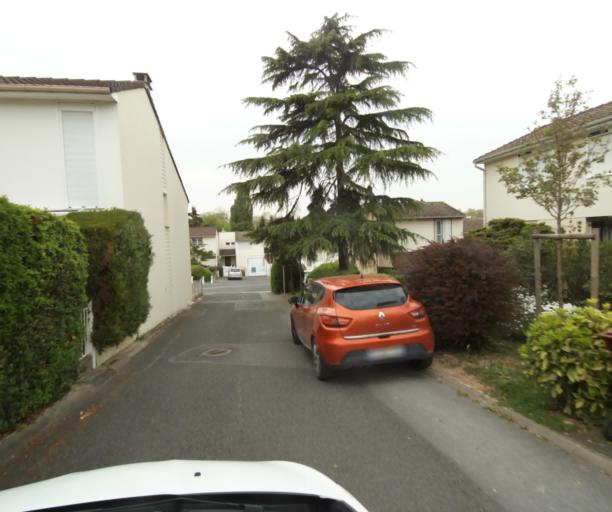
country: FR
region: Ile-de-France
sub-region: Departement de Seine-et-Marne
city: Torcy
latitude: 48.8575
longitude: 2.6573
